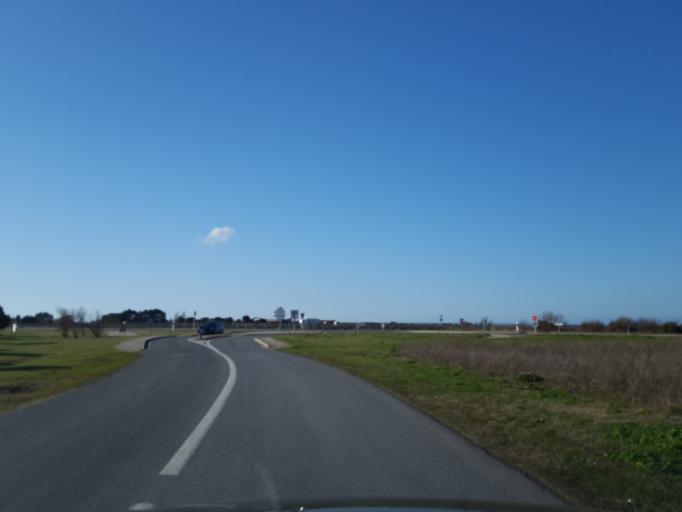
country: FR
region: Poitou-Charentes
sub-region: Departement de la Charente-Maritime
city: La Couarde-sur-Mer
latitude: 46.2223
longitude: -1.4465
